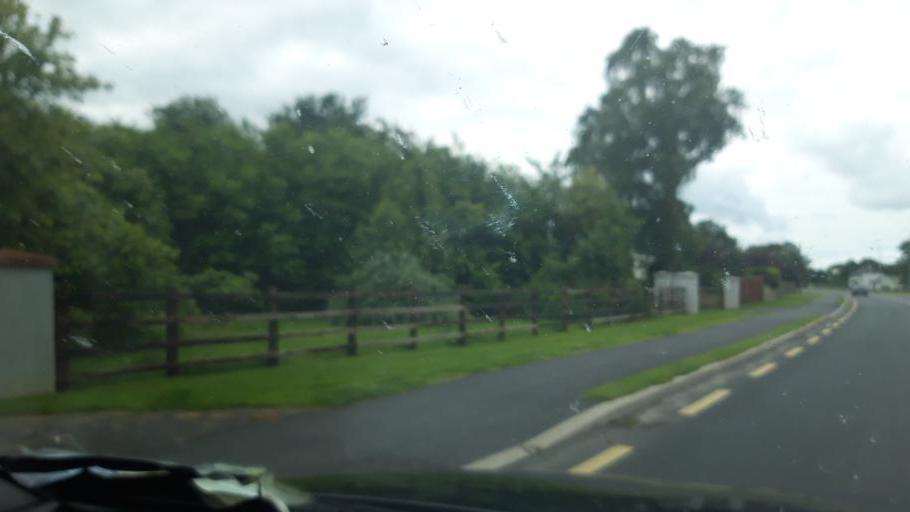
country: IE
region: Leinster
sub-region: Kilkenny
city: Kilkenny
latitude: 52.6264
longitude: -7.2796
